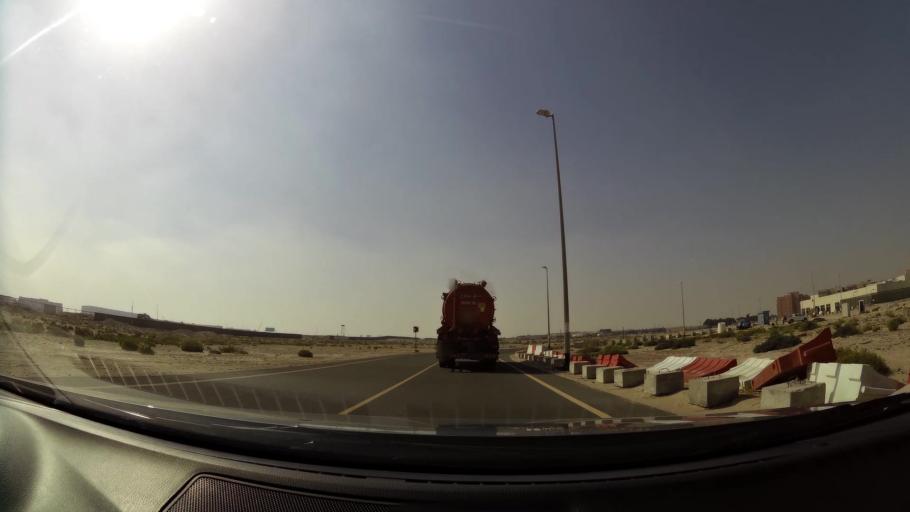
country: AE
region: Dubai
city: Dubai
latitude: 24.9542
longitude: 55.0507
